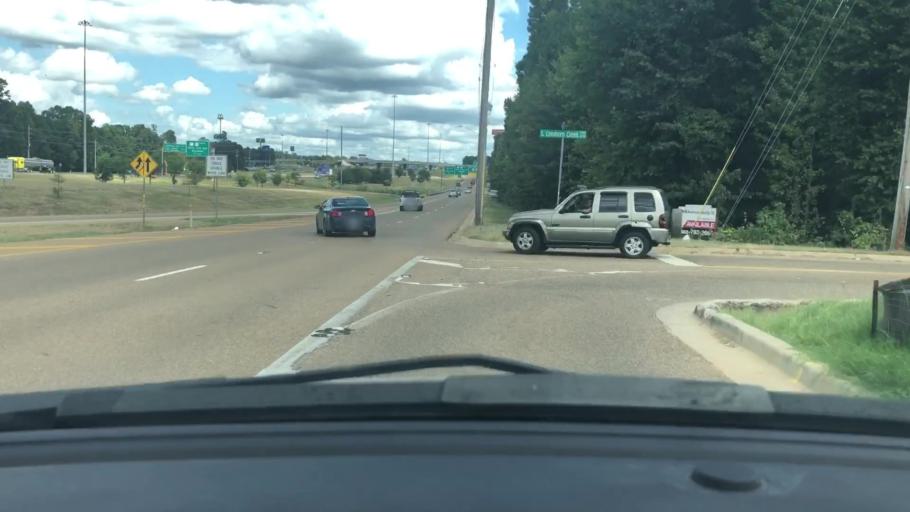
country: US
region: Arkansas
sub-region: Miller County
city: Texarkana
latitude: 33.4609
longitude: -94.0747
